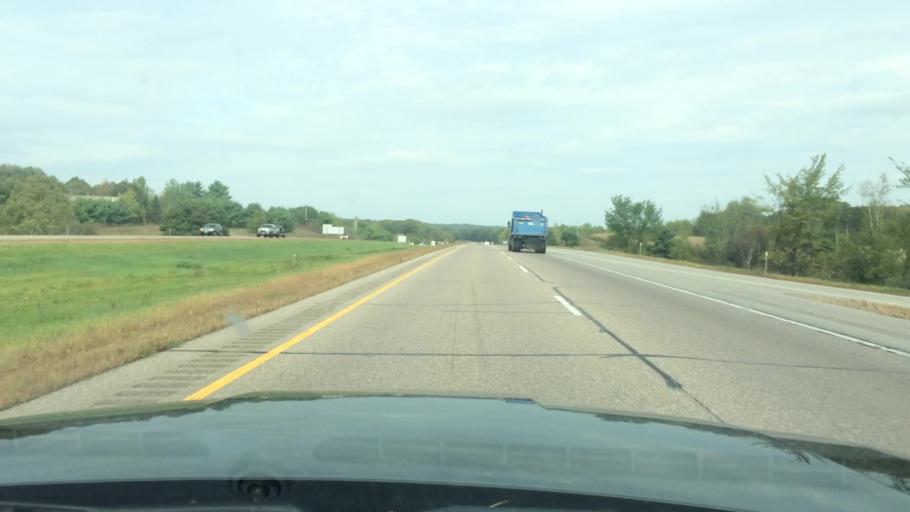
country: US
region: Wisconsin
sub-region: Marathon County
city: Mosinee
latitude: 44.6786
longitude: -89.6415
